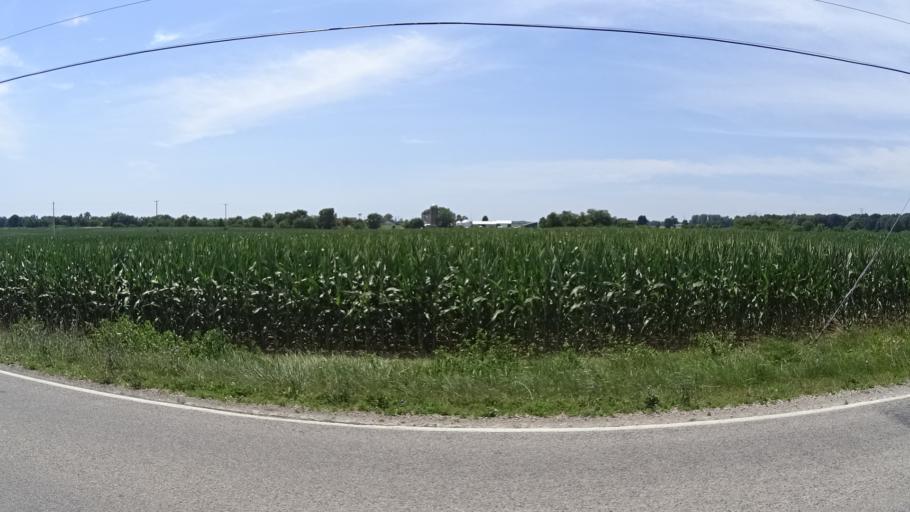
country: US
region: Ohio
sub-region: Erie County
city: Sandusky
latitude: 41.3805
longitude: -82.7704
